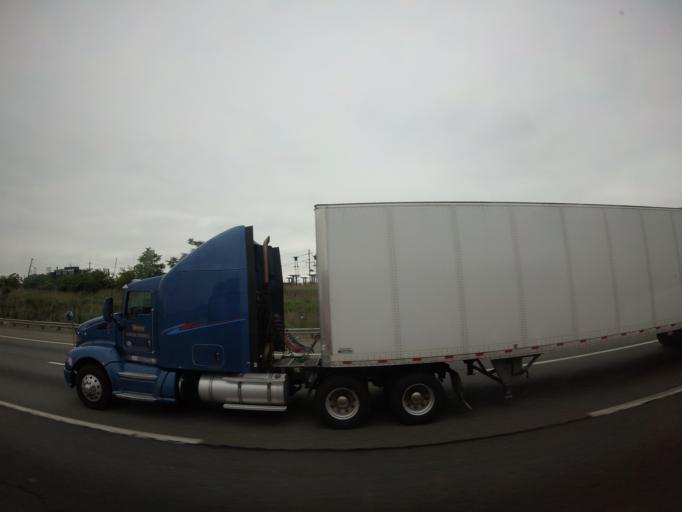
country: US
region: New Jersey
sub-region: Union County
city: Elizabeth
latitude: 40.6796
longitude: -74.1693
